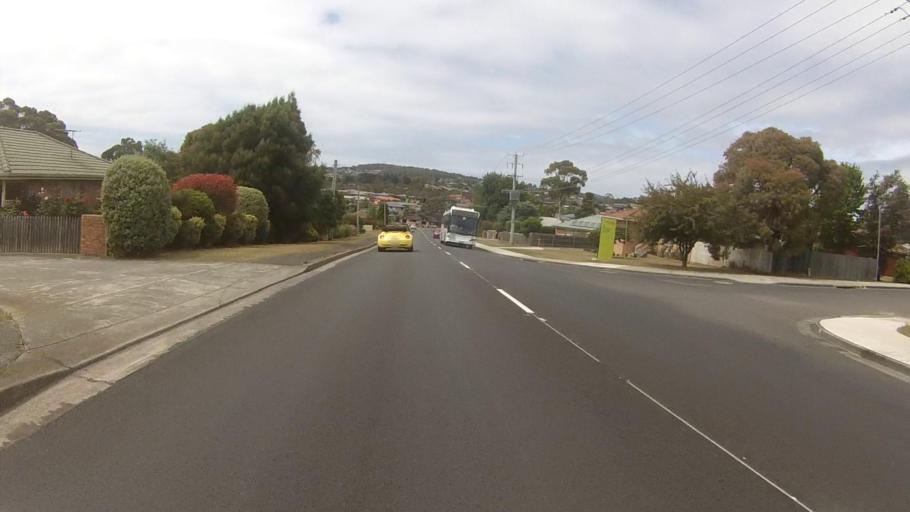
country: AU
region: Tasmania
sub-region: Kingborough
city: Kingston
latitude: -42.9707
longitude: 147.2923
